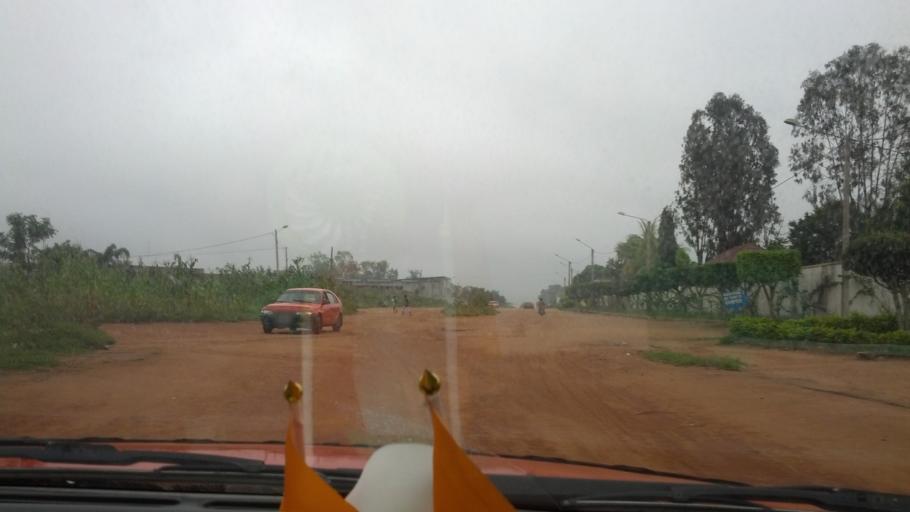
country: CI
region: Vallee du Bandama
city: Bouake
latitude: 7.6919
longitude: -5.0576
